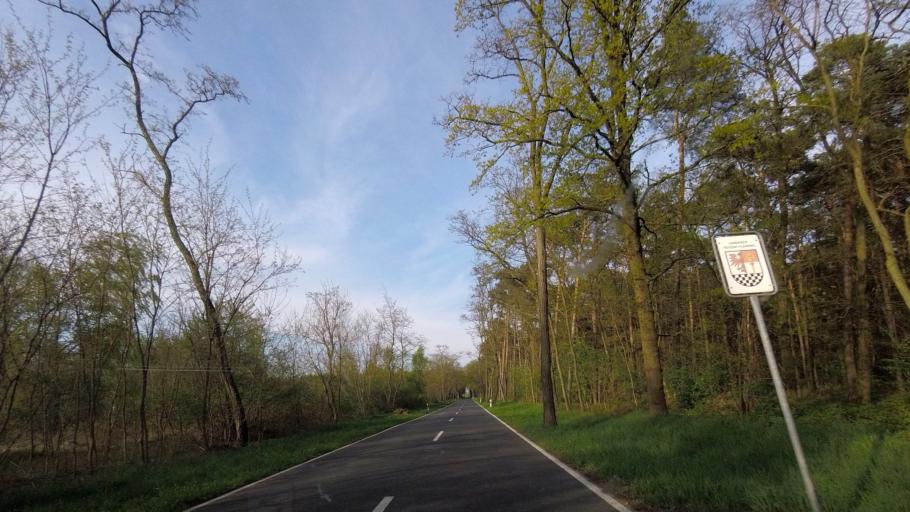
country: DE
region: Saxony-Anhalt
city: Zahna
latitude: 51.9595
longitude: 12.8490
